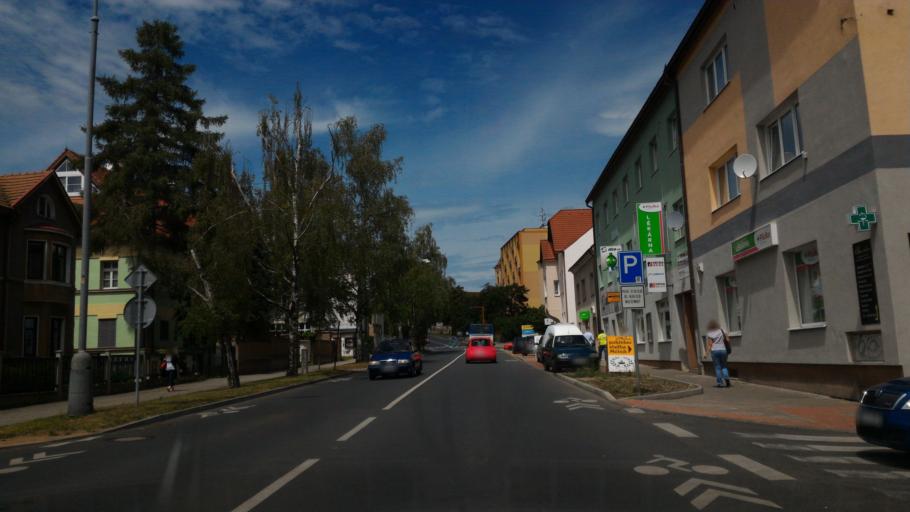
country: CZ
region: Central Bohemia
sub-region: Okres Melnik
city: Melnik
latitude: 50.3477
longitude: 14.4829
